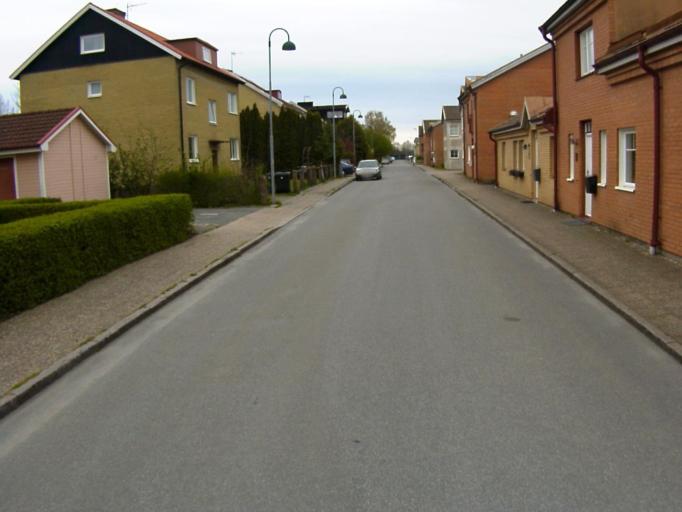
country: SE
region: Skane
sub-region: Kristianstads Kommun
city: Kristianstad
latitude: 56.0203
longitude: 14.1422
